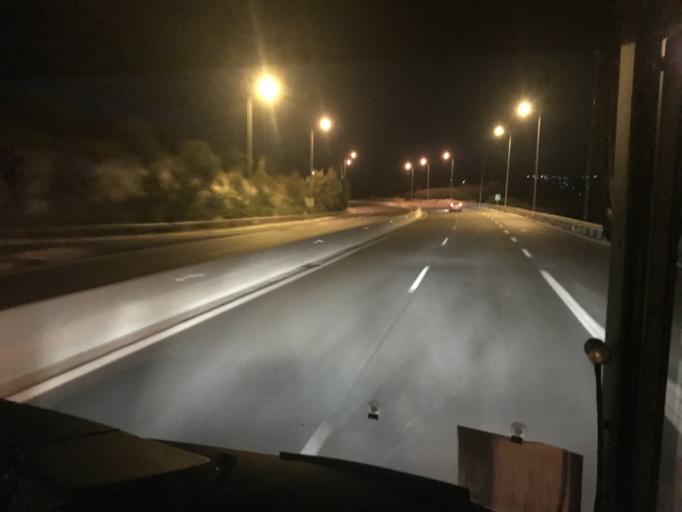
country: GR
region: Crete
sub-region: Nomos Irakleiou
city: Skalanion
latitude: 35.2649
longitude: 25.1836
